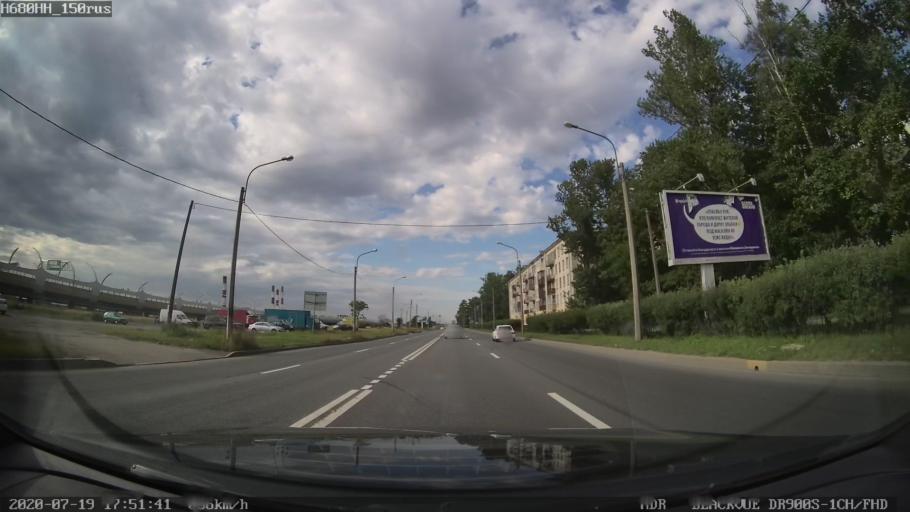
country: RU
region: St.-Petersburg
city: Avtovo
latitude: 59.8595
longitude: 30.2945
